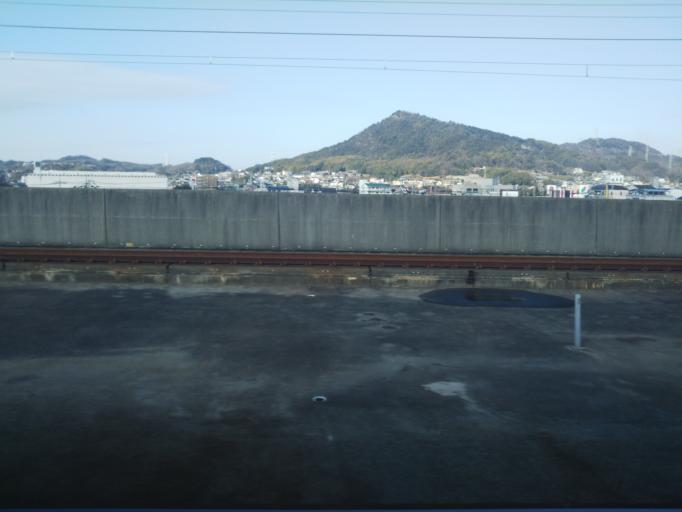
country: JP
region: Okayama
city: Kurashiki
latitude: 34.4603
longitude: 133.8073
